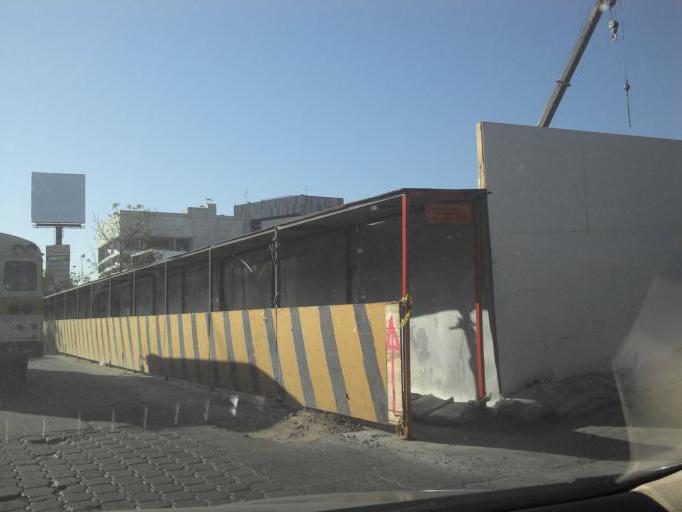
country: MX
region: Baja California
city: Tijuana
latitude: 32.5244
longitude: -117.0215
